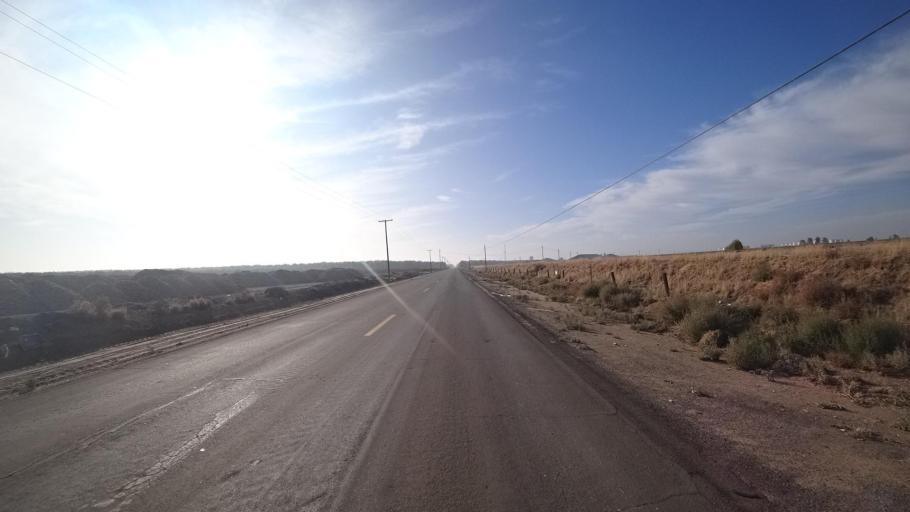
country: US
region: California
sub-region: Kern County
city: McFarland
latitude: 35.6415
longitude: -119.2045
